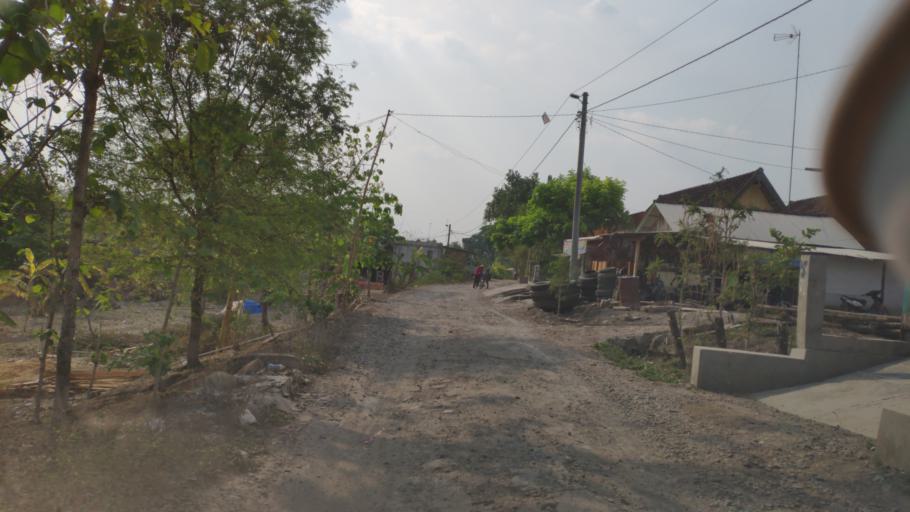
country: ID
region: Central Java
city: Randublatung
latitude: -7.2822
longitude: 111.2515
